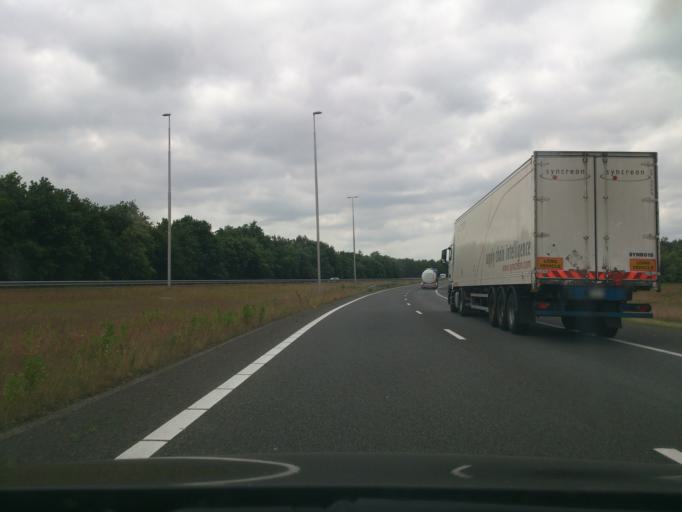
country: NL
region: North Brabant
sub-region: Gemeente Oss
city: Berghem
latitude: 51.7369
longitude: 5.5777
